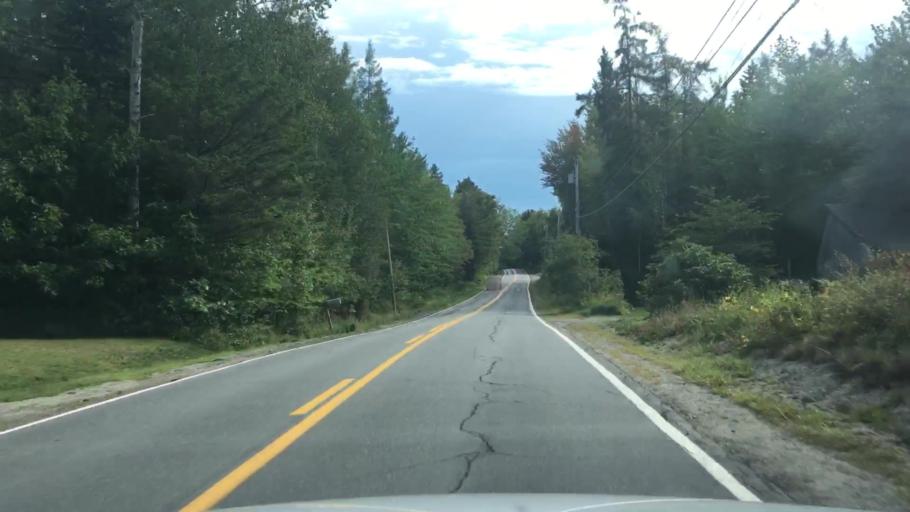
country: US
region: Maine
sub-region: Hancock County
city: Ellsworth
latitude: 44.4830
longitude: -68.4203
